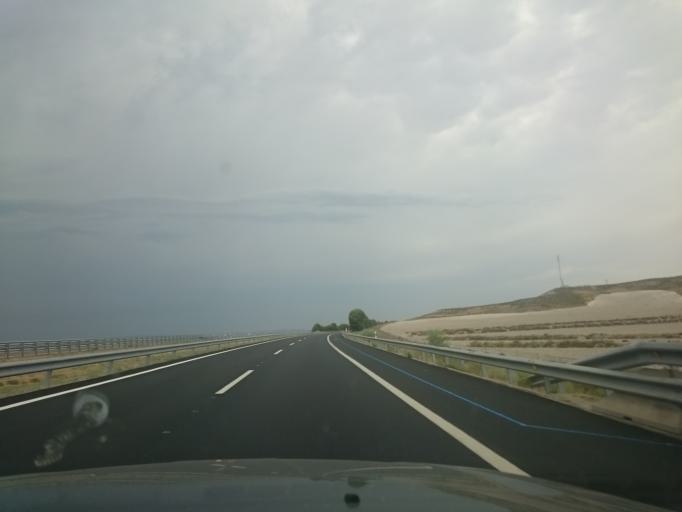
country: ES
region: Aragon
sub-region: Provincia de Zaragoza
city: Pina de Ebro
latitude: 41.5229
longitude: -0.4888
